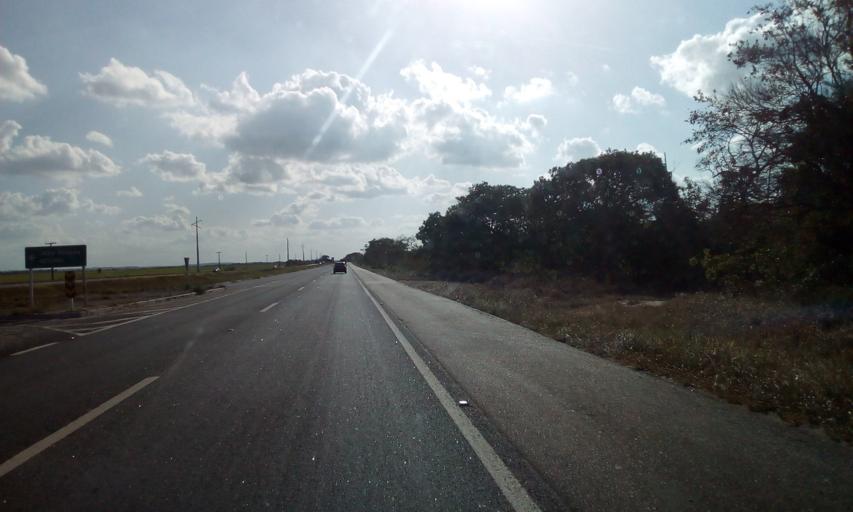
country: BR
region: Paraiba
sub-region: Cruz Do Espirito Santo
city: Cruz do Espirito Santo
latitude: -7.1642
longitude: -35.0261
